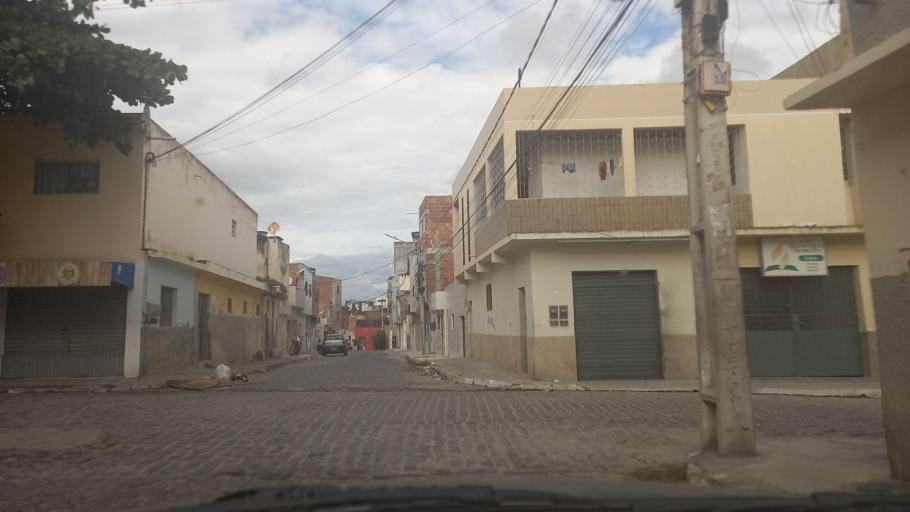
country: BR
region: Pernambuco
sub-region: Caruaru
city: Caruaru
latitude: -8.2917
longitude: -35.9773
